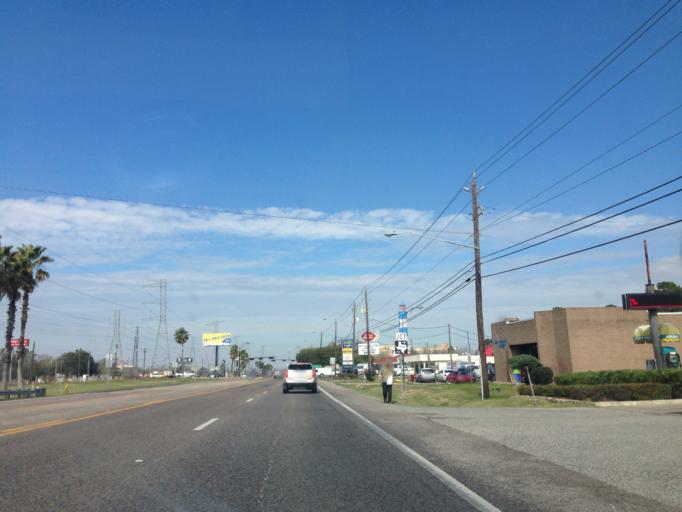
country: US
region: Texas
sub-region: Galveston County
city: Kemah
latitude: 29.5363
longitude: -95.0170
